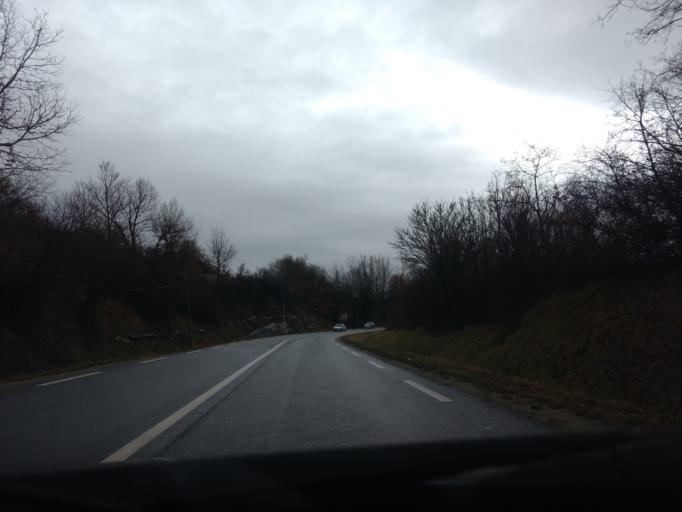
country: FR
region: Midi-Pyrenees
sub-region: Departement de l'Aveyron
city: Firmi
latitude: 44.5107
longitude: 2.3612
